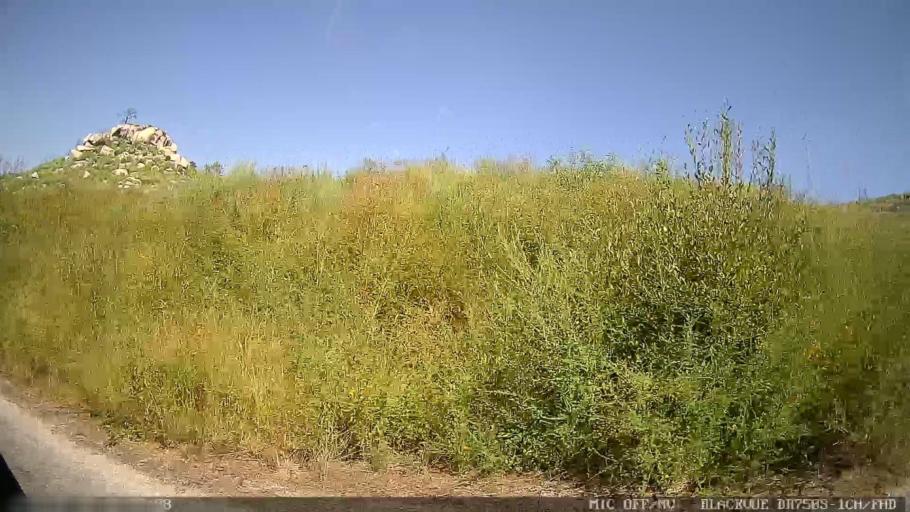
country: PT
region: Vila Real
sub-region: Sabrosa
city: Sabrosa
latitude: 41.3083
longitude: -7.4850
